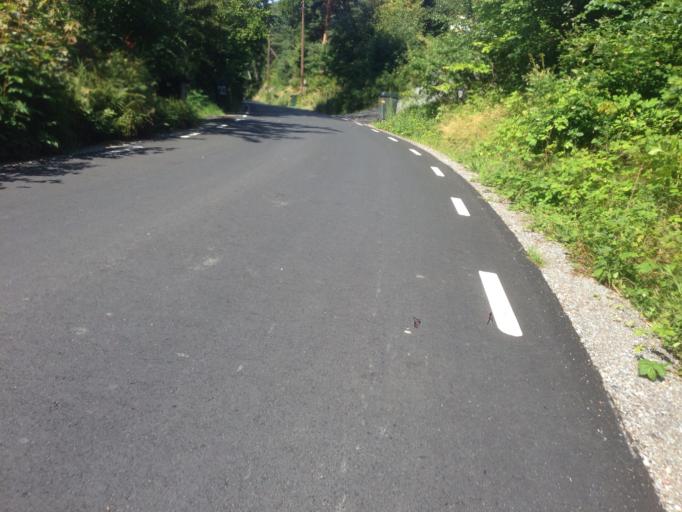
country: SE
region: Stockholm
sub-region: Vaxholms Kommun
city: Vaxholm
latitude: 59.3770
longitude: 18.3892
